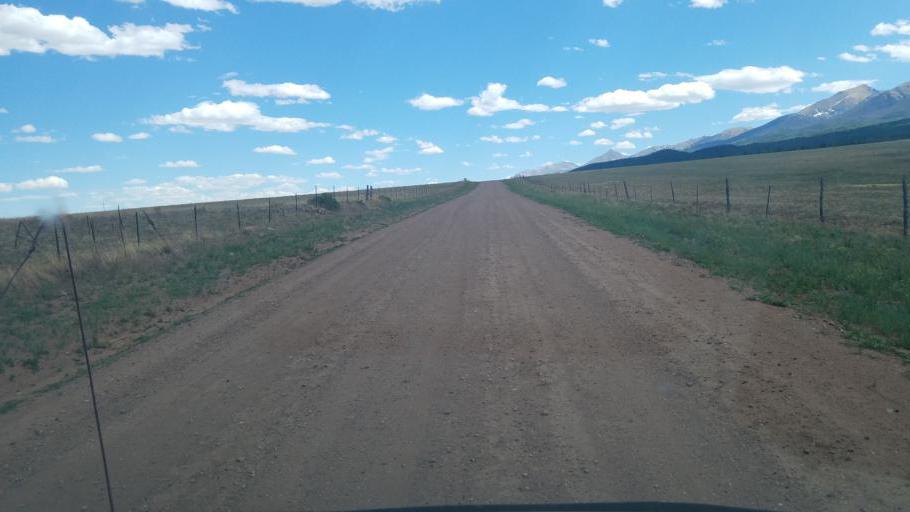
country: US
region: Colorado
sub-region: Custer County
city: Westcliffe
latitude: 38.2492
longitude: -105.6096
